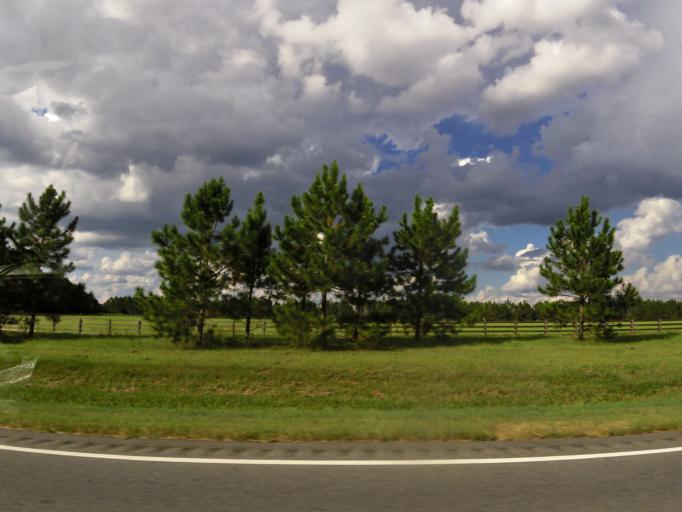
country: US
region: Georgia
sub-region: Lowndes County
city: Remerton
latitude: 30.7999
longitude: -83.3796
